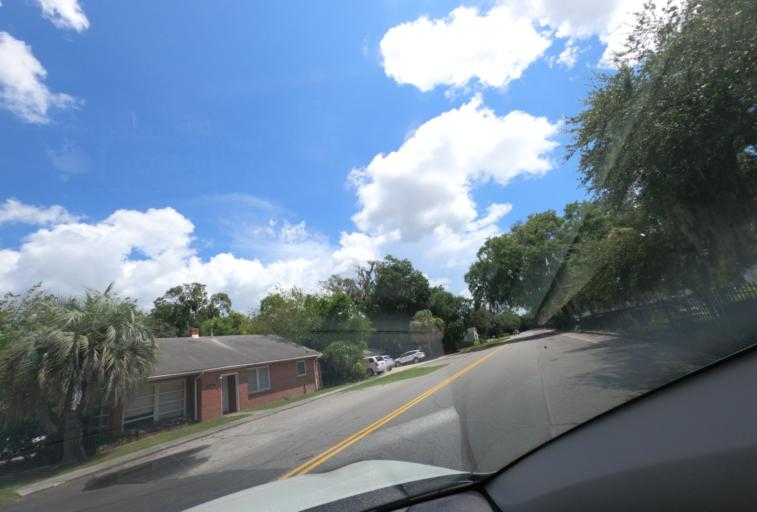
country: US
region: South Carolina
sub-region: Beaufort County
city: Beaufort
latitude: 32.4352
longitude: -80.6740
